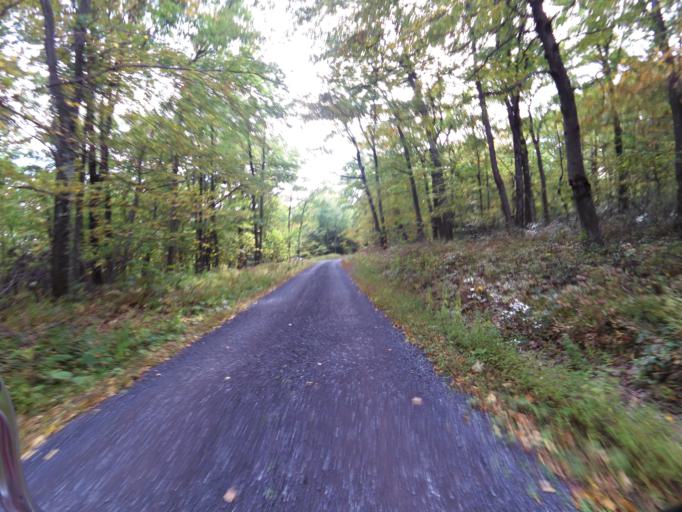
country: US
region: Pennsylvania
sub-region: Lycoming County
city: Jersey Shore
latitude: 41.0930
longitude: -77.1910
